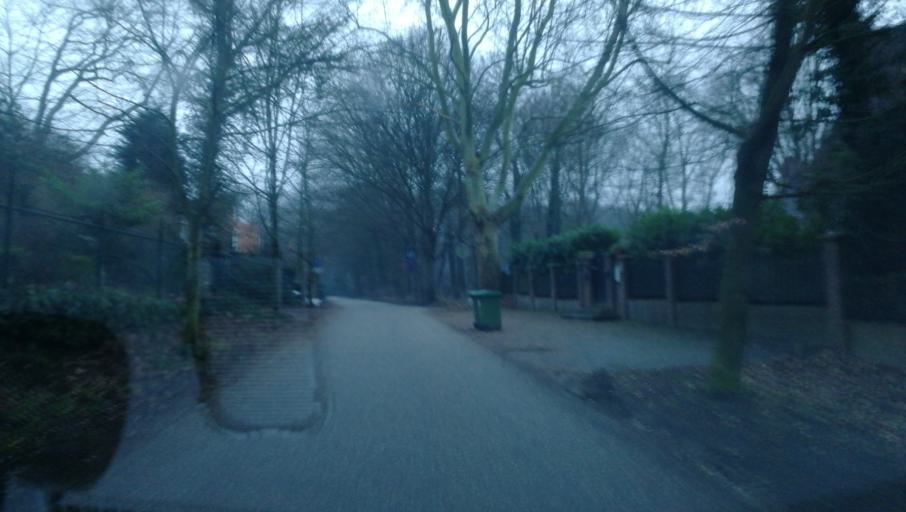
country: NL
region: Limburg
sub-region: Gemeente Venlo
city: Venlo
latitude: 51.3520
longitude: 6.1746
